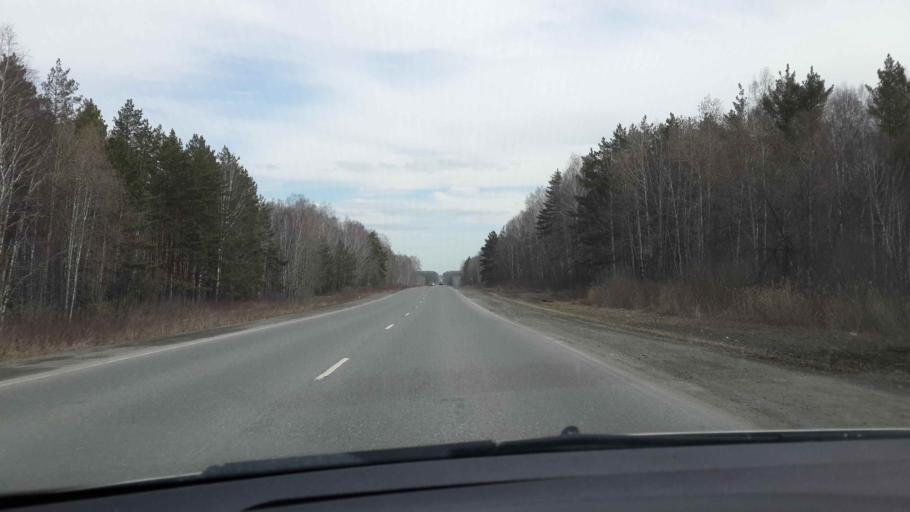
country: RU
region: Sverdlovsk
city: Bogdanovich
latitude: 56.7570
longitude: 62.2701
